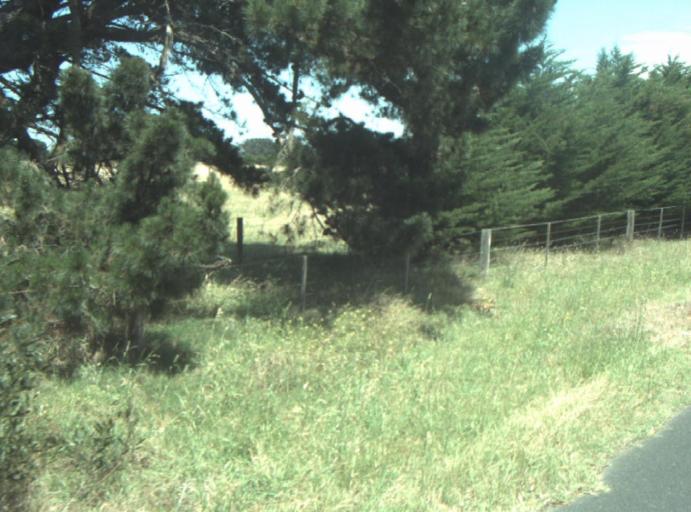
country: AU
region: Victoria
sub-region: Greater Geelong
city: Leopold
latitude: -38.2696
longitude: 144.4720
